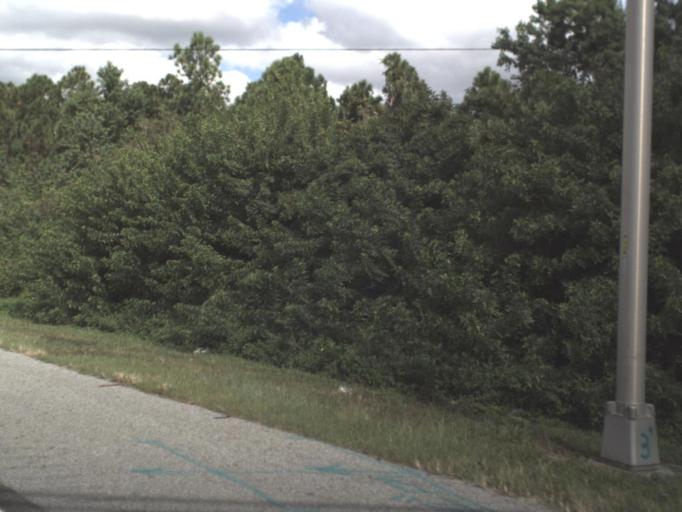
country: US
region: Florida
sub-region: Orange County
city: Oak Ridge
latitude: 28.4506
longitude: -81.4209
